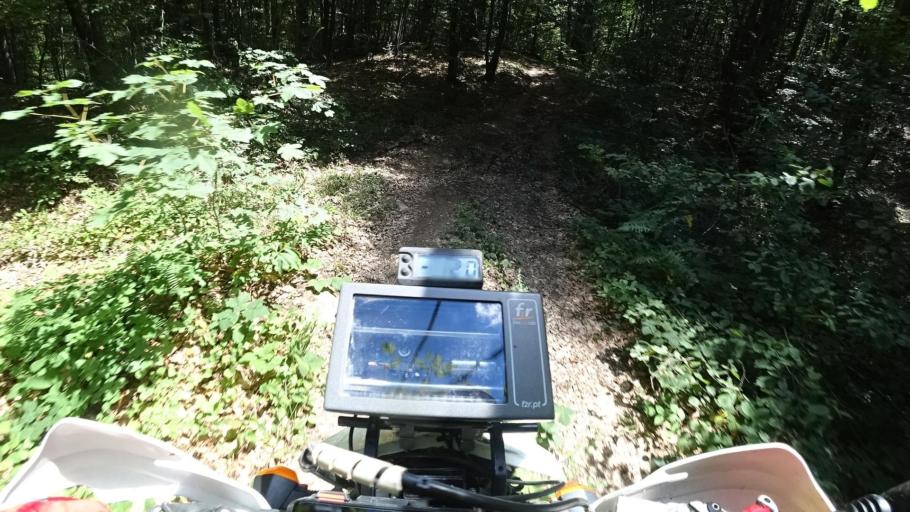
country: HR
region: Karlovacka
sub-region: Grad Ogulin
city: Ogulin
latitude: 45.2299
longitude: 15.1884
